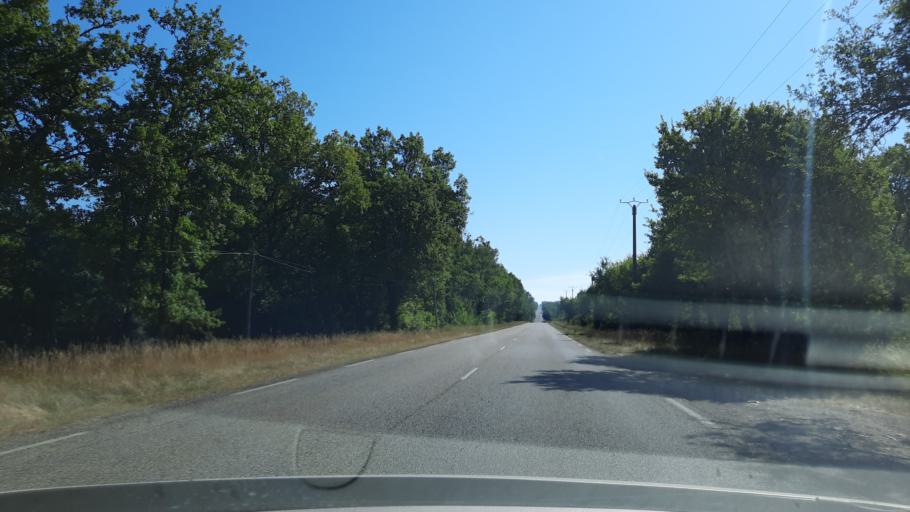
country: FR
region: Midi-Pyrenees
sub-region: Departement du Tarn-et-Garonne
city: Septfonds
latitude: 44.1828
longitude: 1.6417
